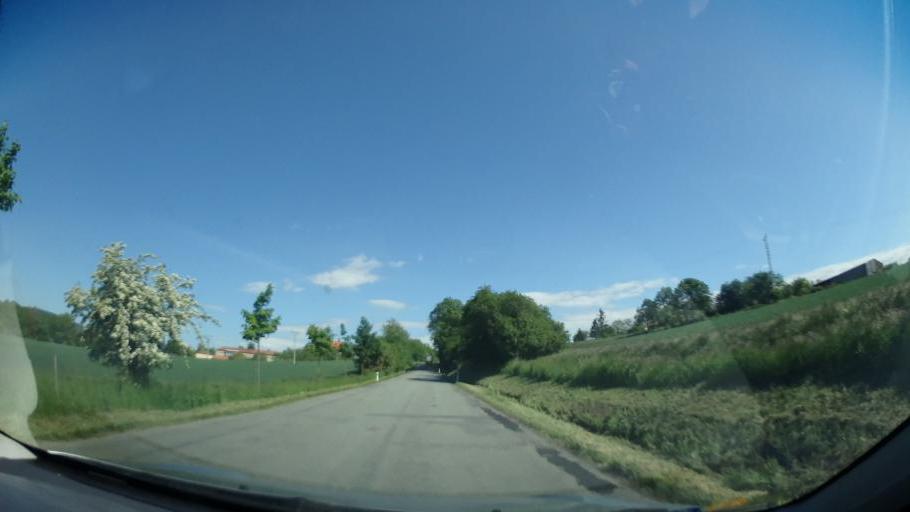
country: CZ
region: South Moravian
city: Velke Opatovice
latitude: 49.6762
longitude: 16.6305
